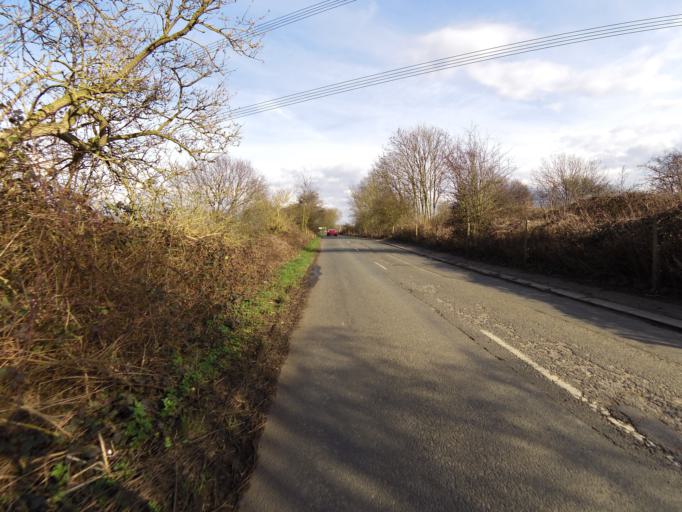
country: GB
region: England
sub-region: East Riding of Yorkshire
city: Snaith
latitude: 53.6912
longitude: -1.0454
